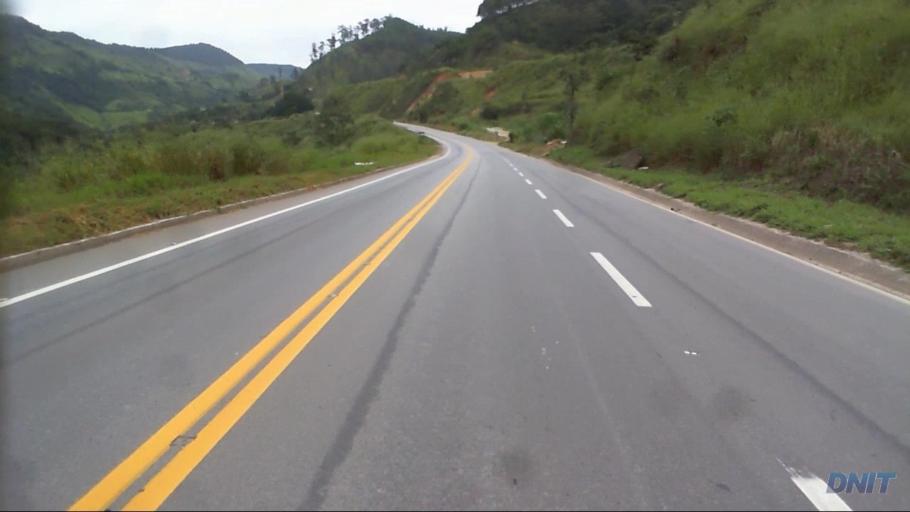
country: BR
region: Minas Gerais
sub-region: Timoteo
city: Timoteo
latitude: -19.6237
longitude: -42.8047
